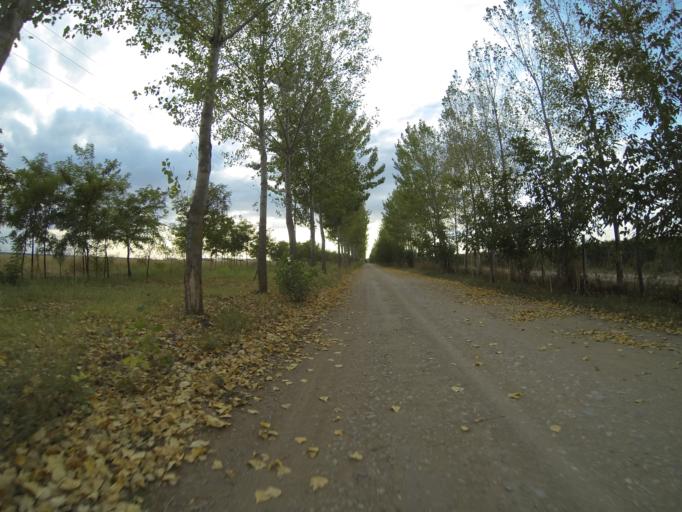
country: RO
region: Dolj
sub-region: Comuna Segarcea
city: Segarcea
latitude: 44.1046
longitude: 23.7040
